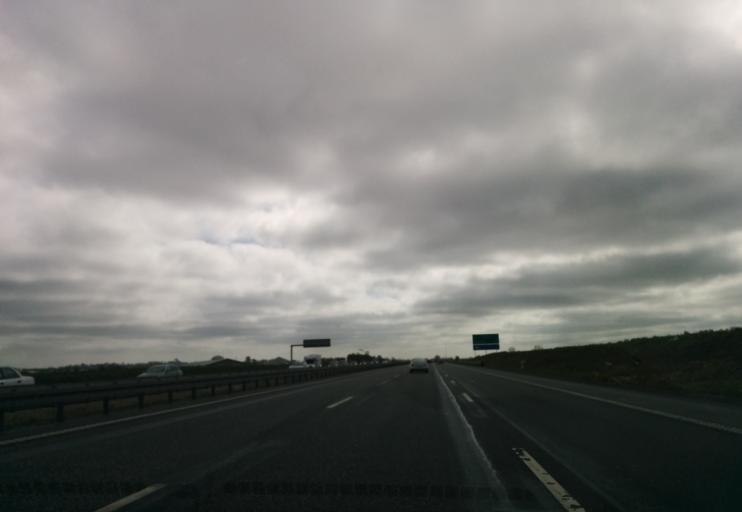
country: DK
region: South Denmark
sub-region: Middelfart Kommune
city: Norre Aby
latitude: 55.4907
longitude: 9.8287
